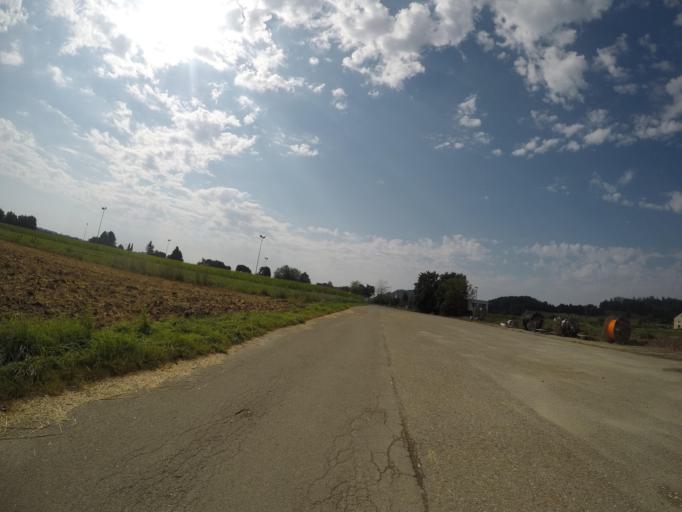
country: DE
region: Baden-Wuerttemberg
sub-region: Tuebingen Region
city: Dietenheim
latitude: 48.1738
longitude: 10.0781
